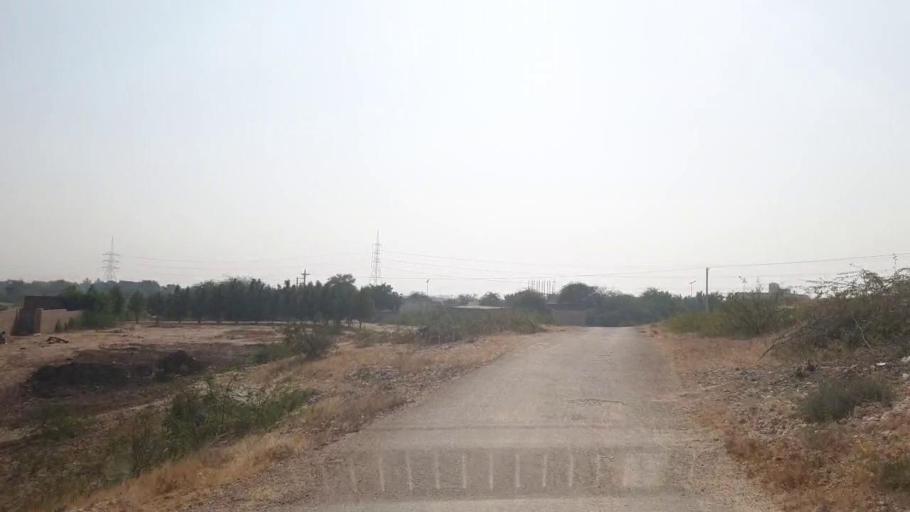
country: PK
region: Sindh
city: Kotri
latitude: 25.3188
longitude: 68.2689
